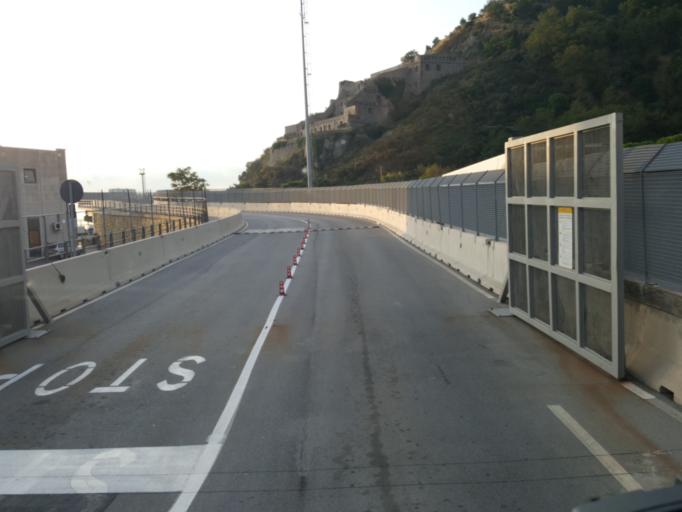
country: IT
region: Liguria
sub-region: Provincia di Savona
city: Bergeggi
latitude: 44.2630
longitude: 8.4478
